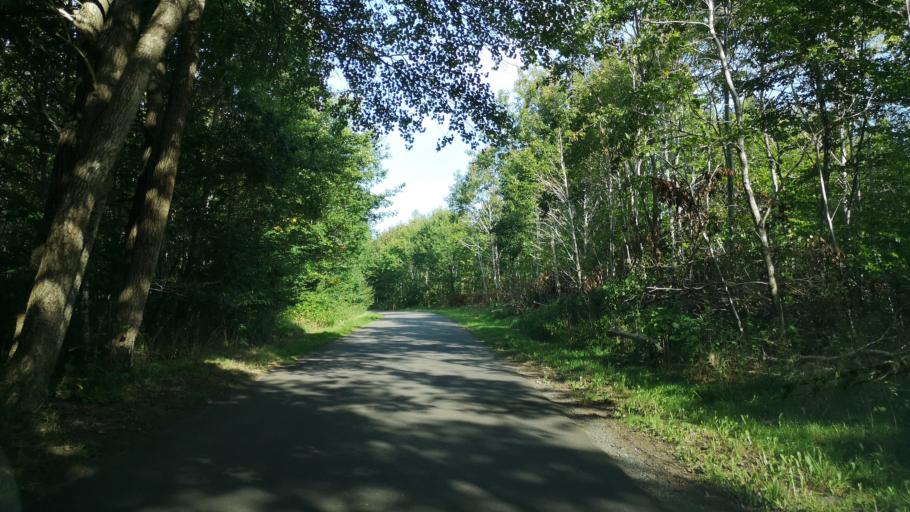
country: DK
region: Central Jutland
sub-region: Herning Kommune
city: Herning
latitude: 56.1728
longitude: 8.9586
